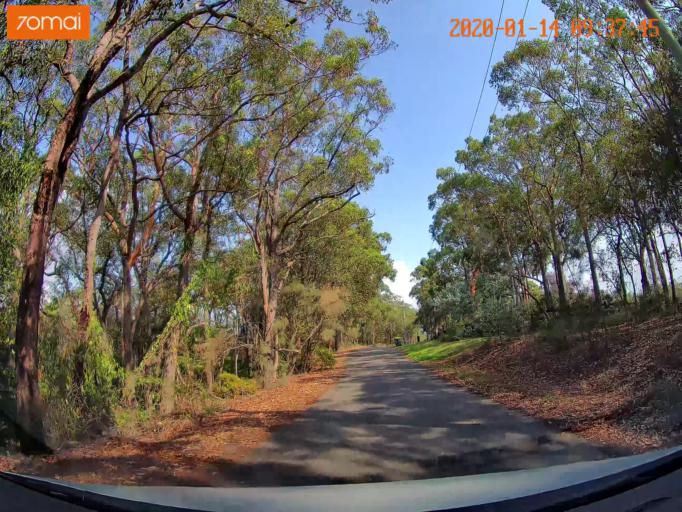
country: AU
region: New South Wales
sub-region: Wyong Shire
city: Kingfisher Shores
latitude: -33.1150
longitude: 151.5588
